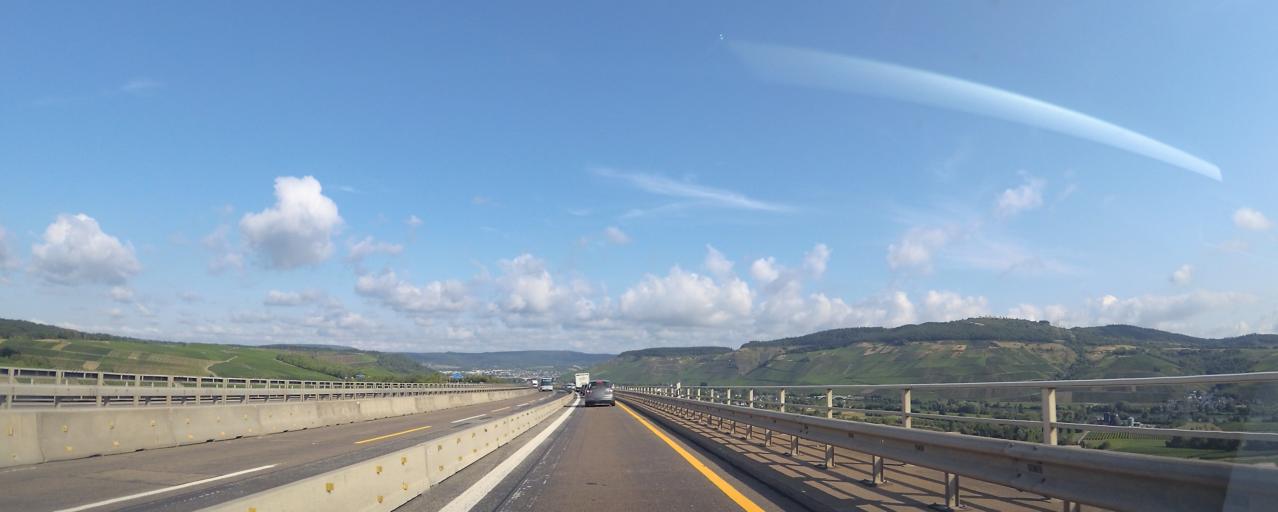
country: DE
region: Rheinland-Pfalz
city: Longuich
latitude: 49.7932
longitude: 6.7775
